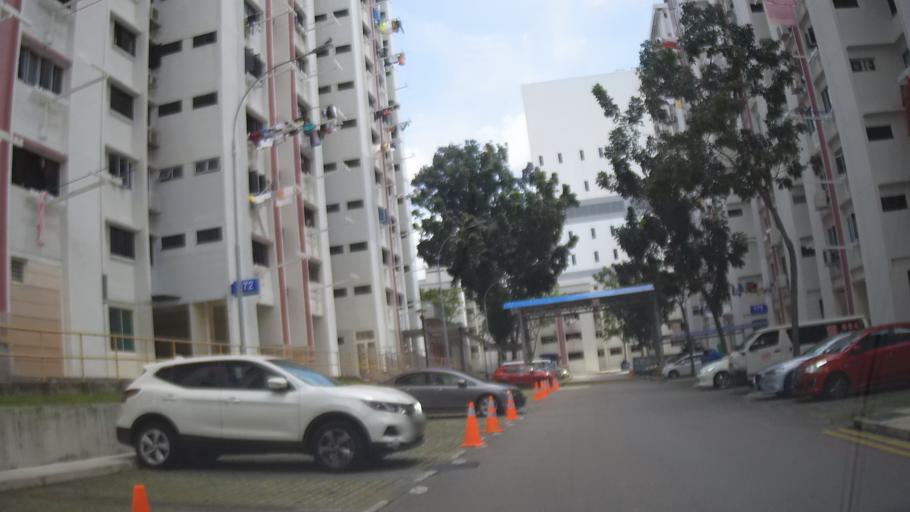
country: MY
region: Johor
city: Johor Bahru
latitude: 1.4337
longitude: 103.7771
